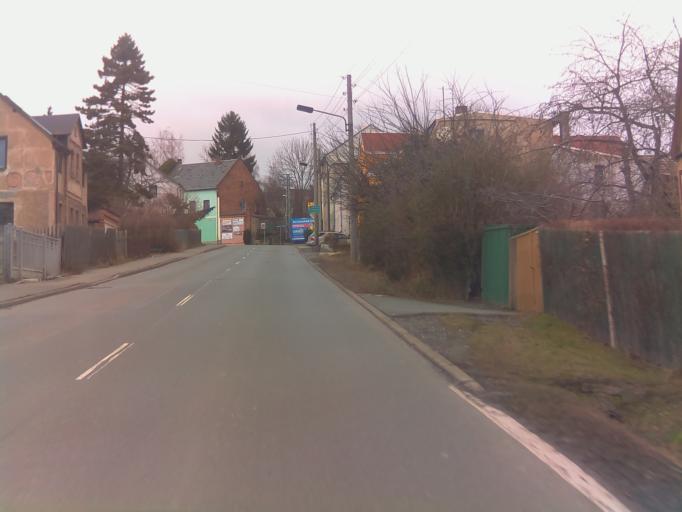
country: DE
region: Thuringia
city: Zeulenroda
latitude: 50.6435
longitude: 11.9867
